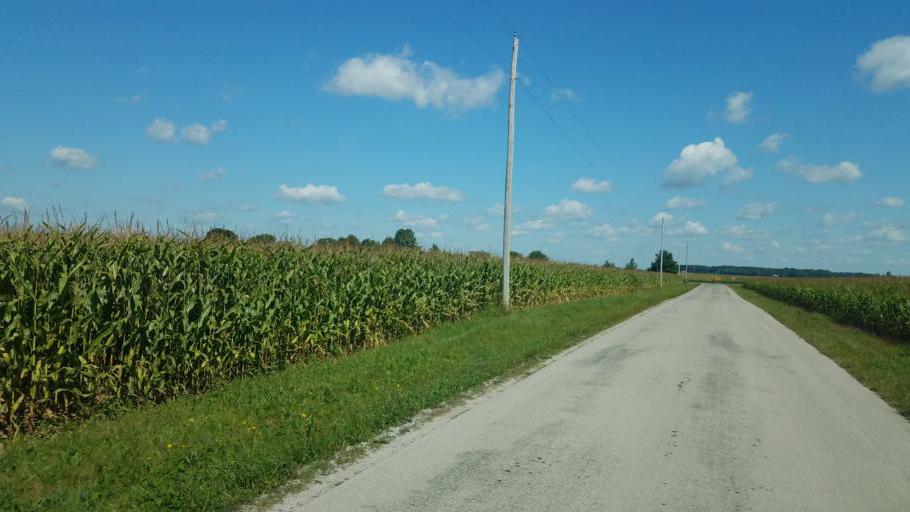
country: US
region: Ohio
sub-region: Wyandot County
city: Carey
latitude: 40.9824
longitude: -83.3339
